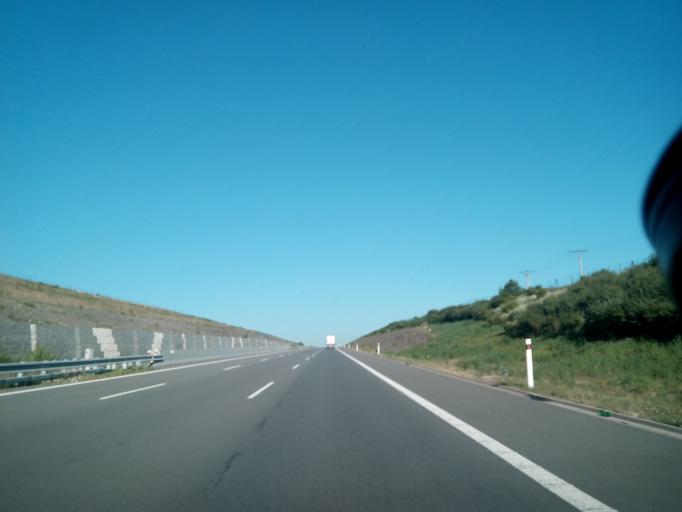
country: SK
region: Presovsky
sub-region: Okres Presov
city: Presov
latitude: 49.0043
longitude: 21.1557
